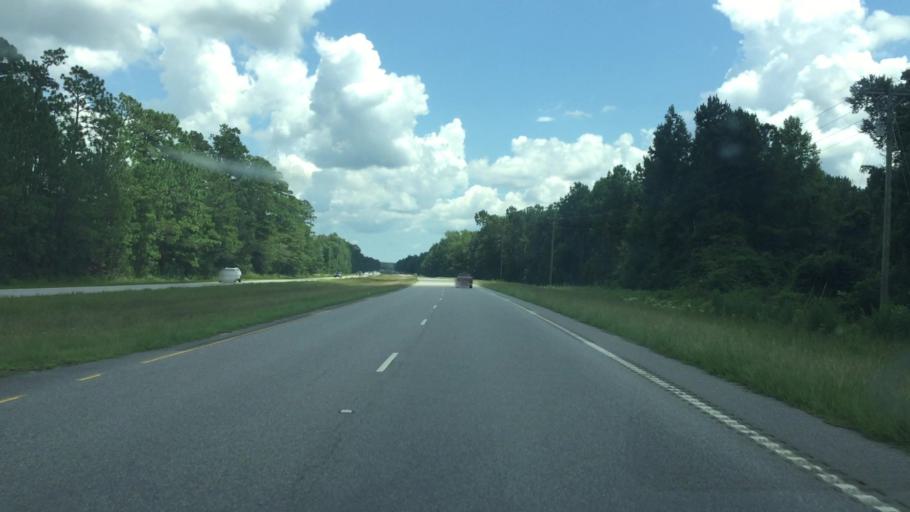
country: US
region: South Carolina
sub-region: Horry County
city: Loris
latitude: 34.0464
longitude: -78.8319
